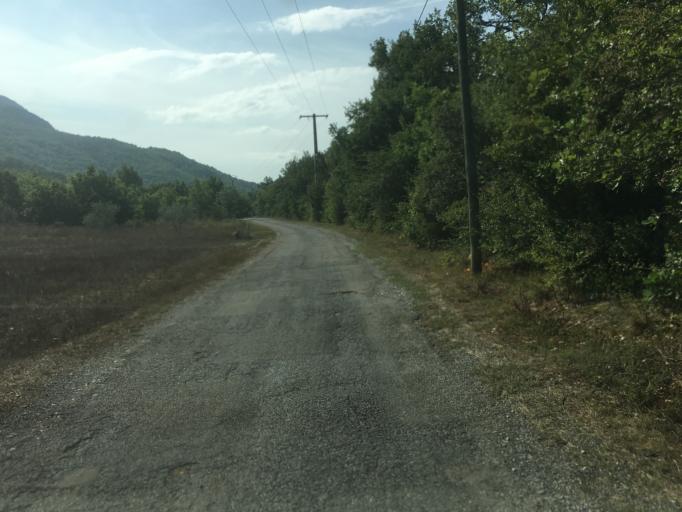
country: FR
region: Provence-Alpes-Cote d'Azur
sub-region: Departement des Alpes-de-Haute-Provence
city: Mallemoisson
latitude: 43.9323
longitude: 6.1877
